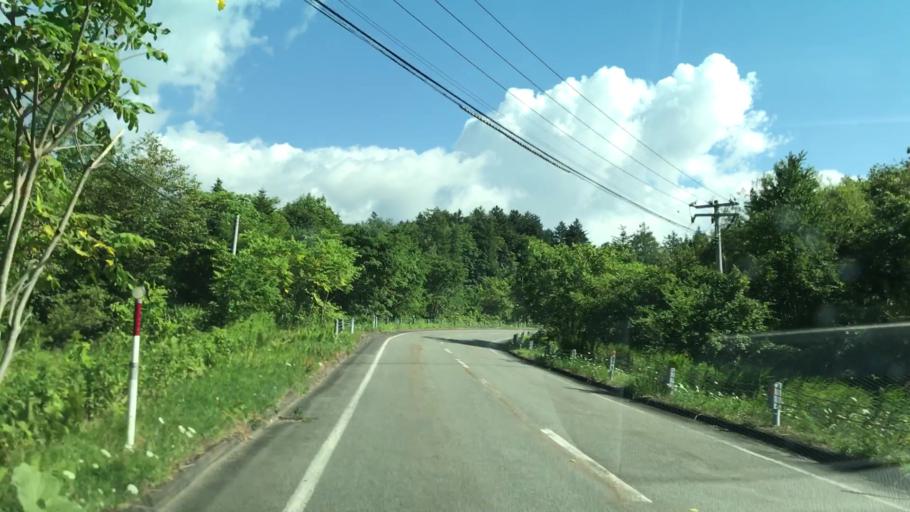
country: JP
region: Hokkaido
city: Shimo-furano
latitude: 42.8639
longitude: 142.4404
